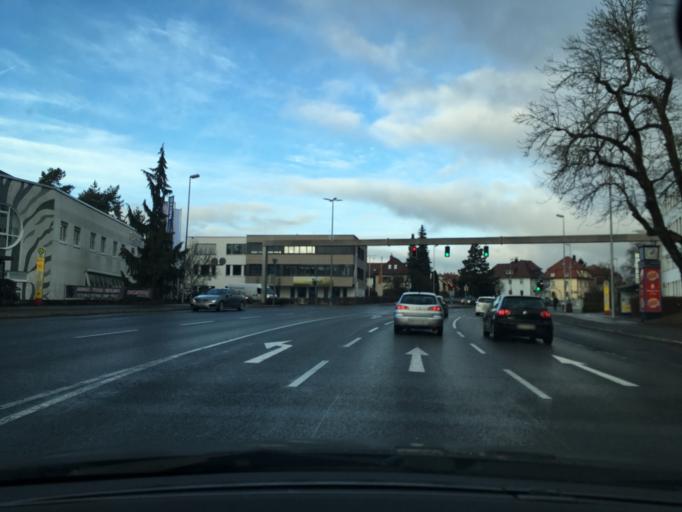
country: DE
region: Baden-Wuerttemberg
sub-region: Tuebingen Region
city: Weingarten
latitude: 47.8003
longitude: 9.6318
